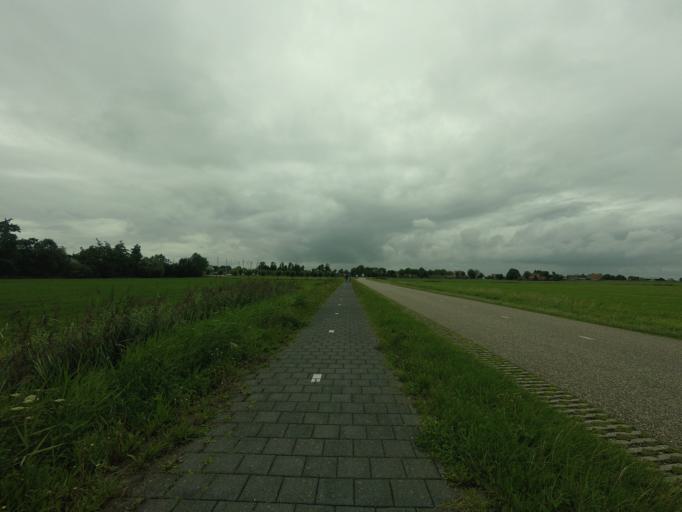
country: NL
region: Friesland
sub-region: Sudwest Fryslan
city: Heeg
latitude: 52.9679
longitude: 5.5447
